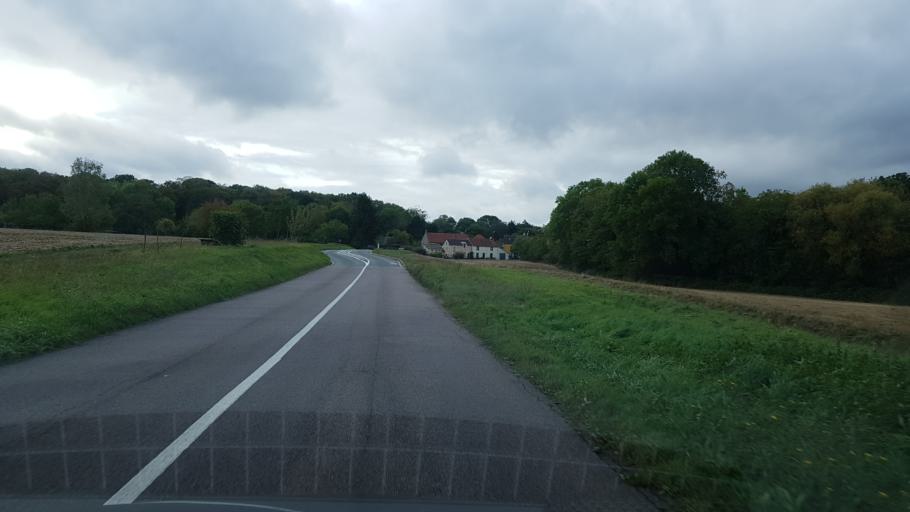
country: FR
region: Ile-de-France
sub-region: Departement de l'Essonne
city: Fontenay-les-Briis
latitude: 48.6453
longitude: 2.1591
